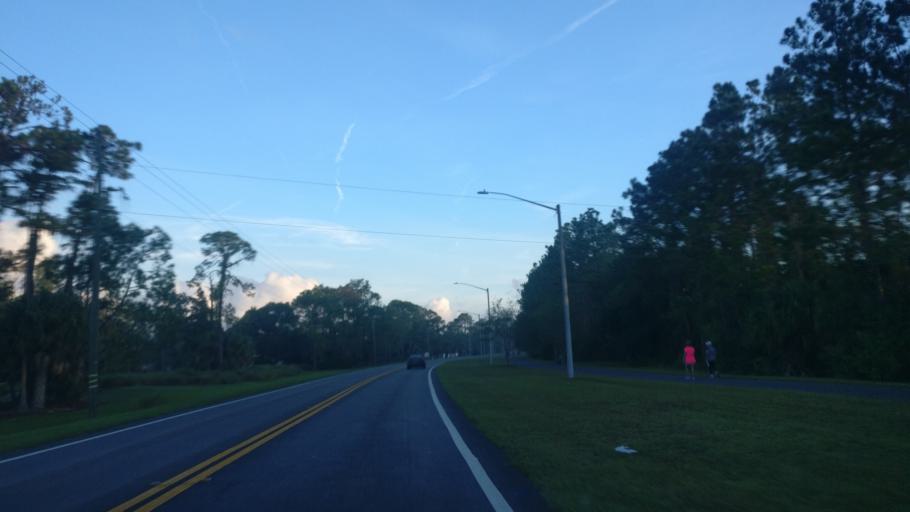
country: US
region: Florida
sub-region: Flagler County
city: Palm Coast
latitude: 29.5352
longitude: -81.2388
